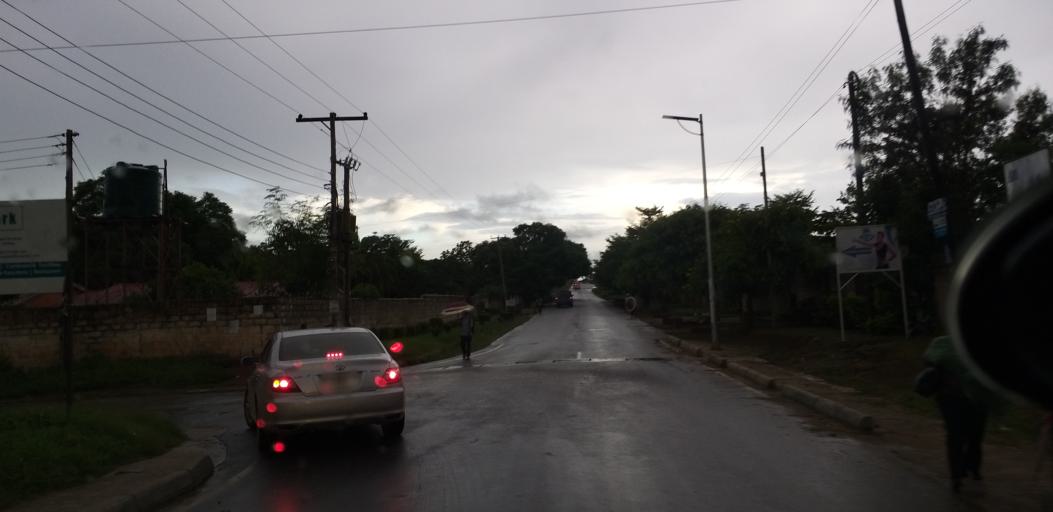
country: ZM
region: Lusaka
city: Lusaka
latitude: -15.4177
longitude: 28.3656
